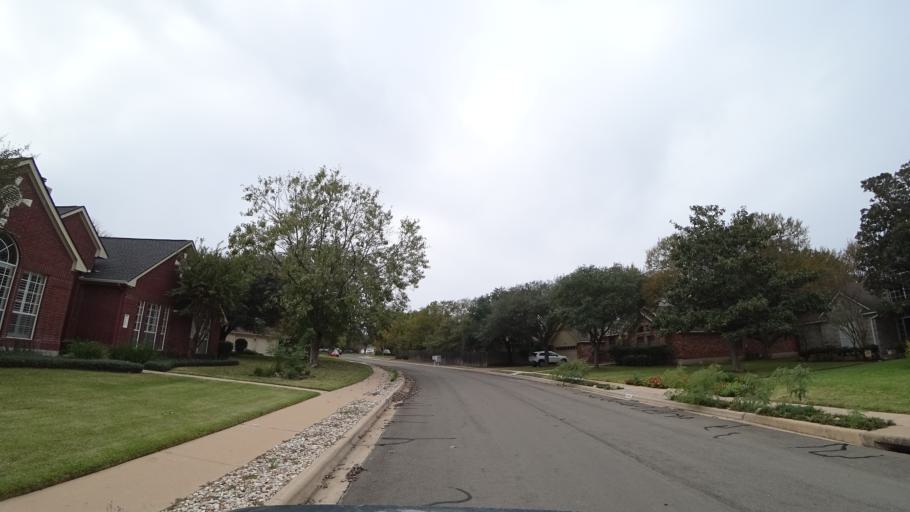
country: US
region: Texas
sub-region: Williamson County
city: Round Rock
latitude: 30.5168
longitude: -97.7043
